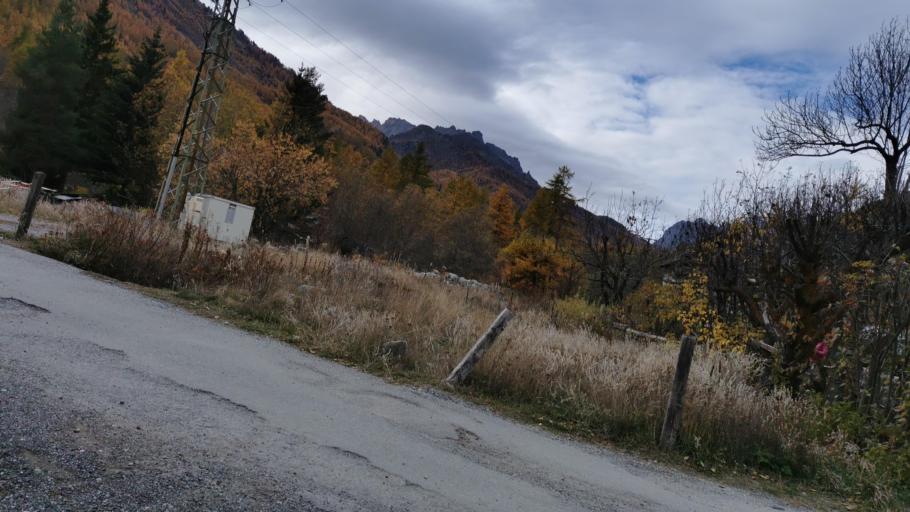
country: FR
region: Provence-Alpes-Cote d'Azur
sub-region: Departement des Hautes-Alpes
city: Villeneuve
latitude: 45.0182
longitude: 6.6048
